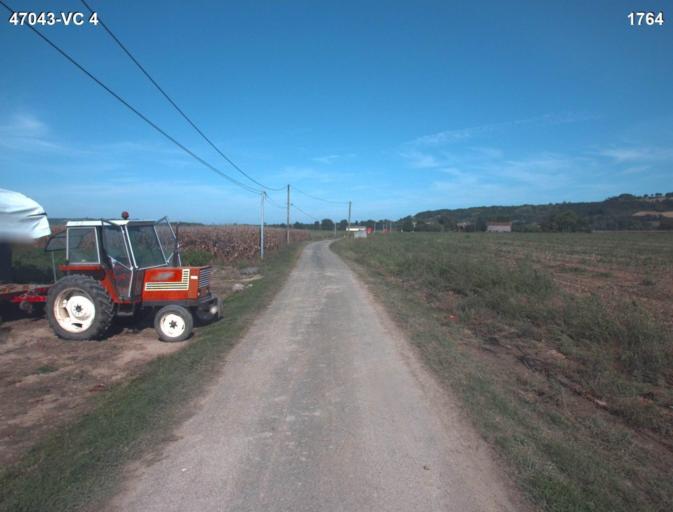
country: FR
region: Aquitaine
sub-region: Departement du Lot-et-Garonne
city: Buzet-sur-Baise
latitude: 44.2693
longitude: 0.3212
